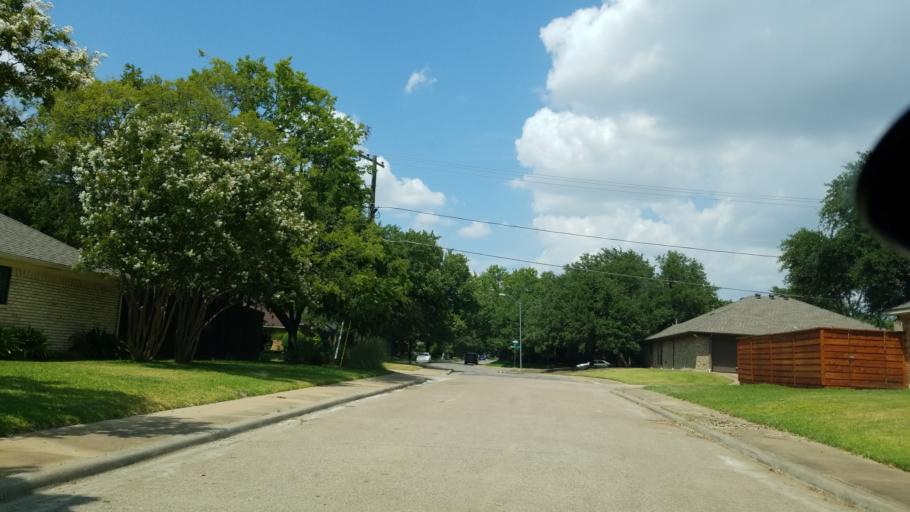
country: US
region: Texas
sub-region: Dallas County
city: Richardson
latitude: 32.9164
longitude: -96.7217
